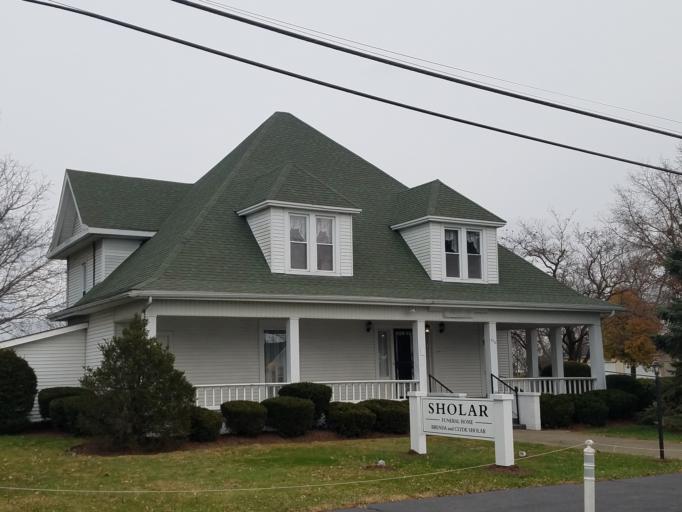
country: US
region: Kentucky
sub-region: Henry County
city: Eminence
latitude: 38.3590
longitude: -85.1048
